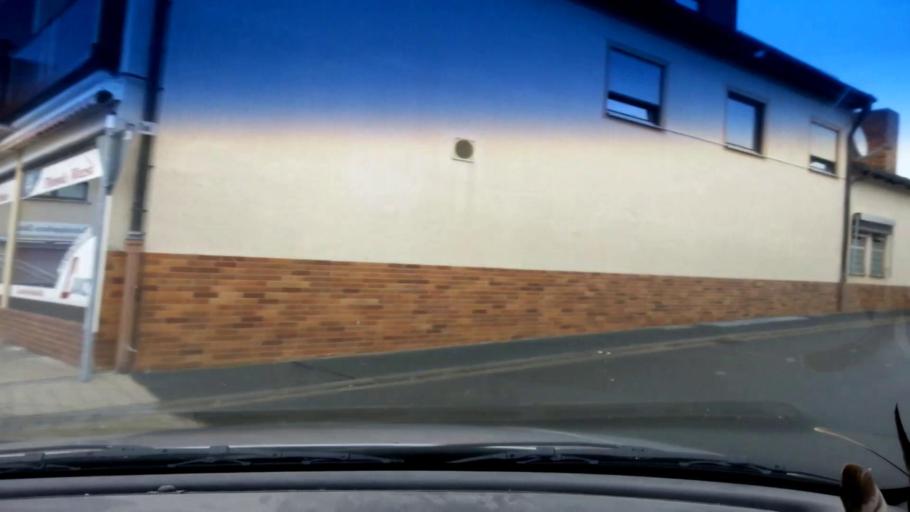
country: DE
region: Bavaria
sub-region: Upper Franconia
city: Litzendorf
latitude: 49.9106
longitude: 11.0103
